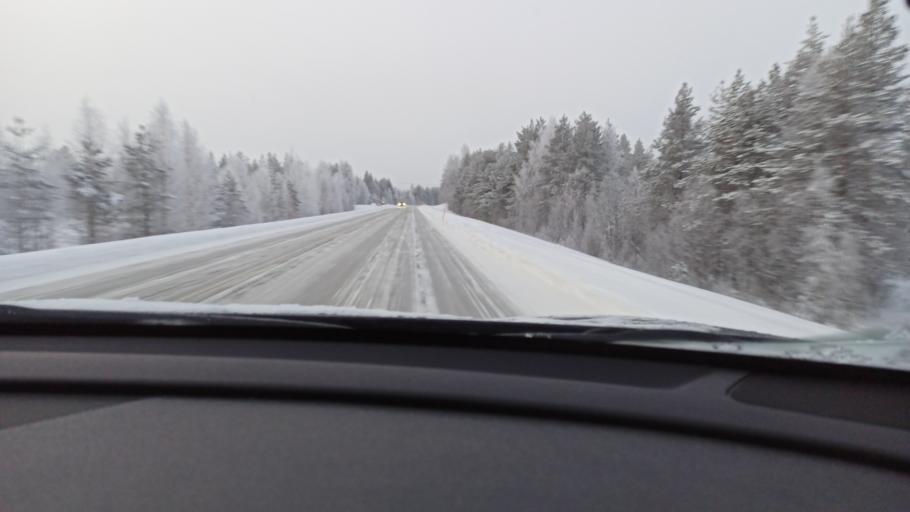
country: FI
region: Lapland
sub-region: Pohjois-Lappi
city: Sodankylae
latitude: 66.9326
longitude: 26.2625
